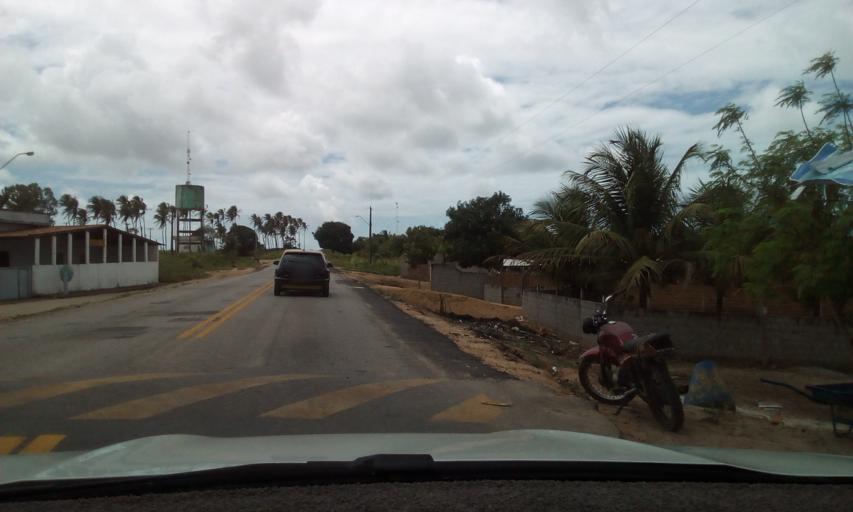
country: BR
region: Paraiba
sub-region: Rio Tinto
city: Rio Tinto
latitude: -6.7708
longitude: -35.0098
